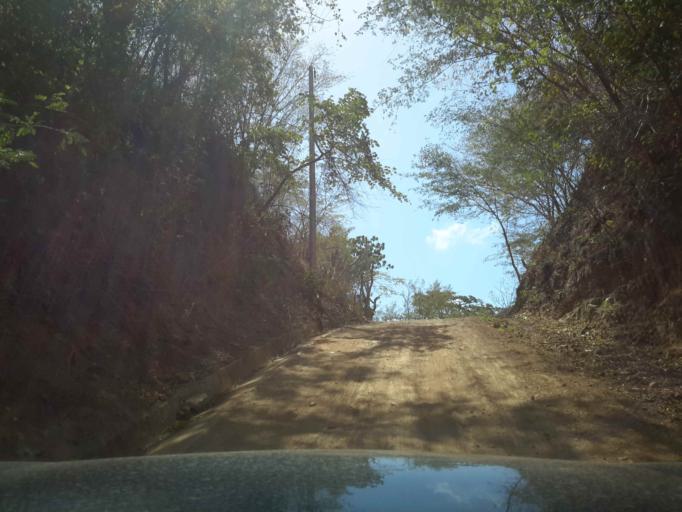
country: NI
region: Rivas
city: San Juan del Sur
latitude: 11.1826
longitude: -85.8113
